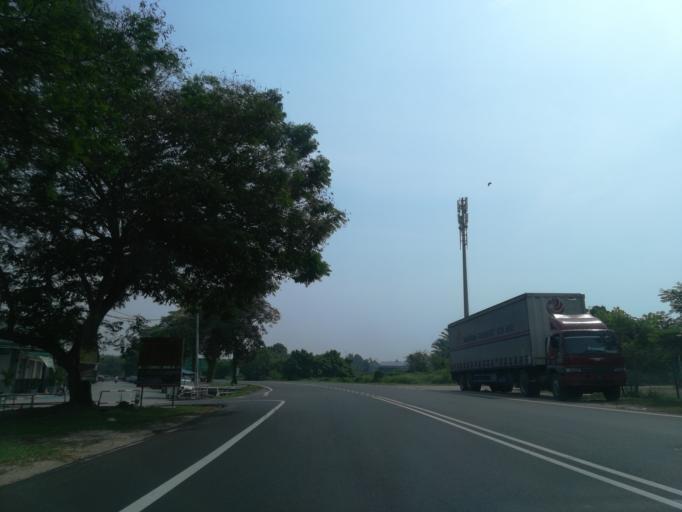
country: MY
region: Kedah
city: Kulim
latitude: 5.4253
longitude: 100.5524
